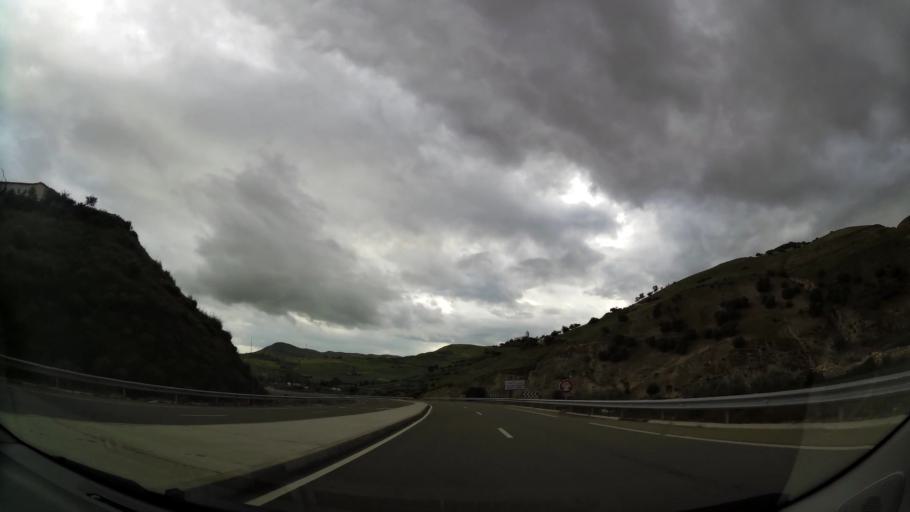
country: MA
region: Taza-Al Hoceima-Taounate
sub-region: Taza
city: Taza
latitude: 34.3113
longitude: -3.9652
